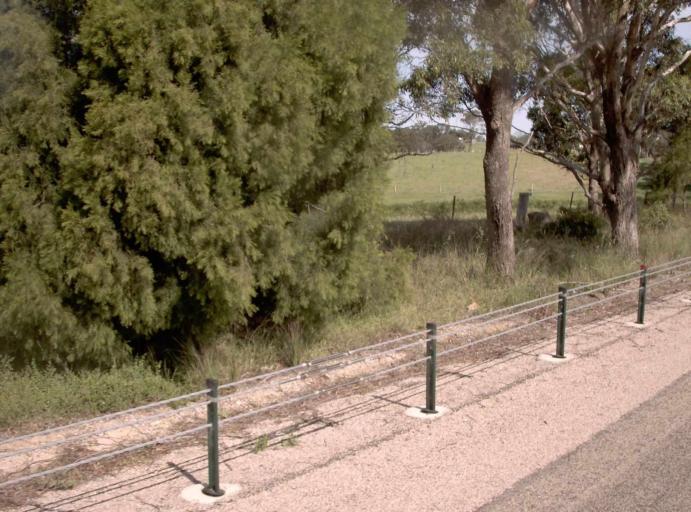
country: AU
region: Victoria
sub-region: East Gippsland
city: Lakes Entrance
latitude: -37.8445
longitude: 147.9292
